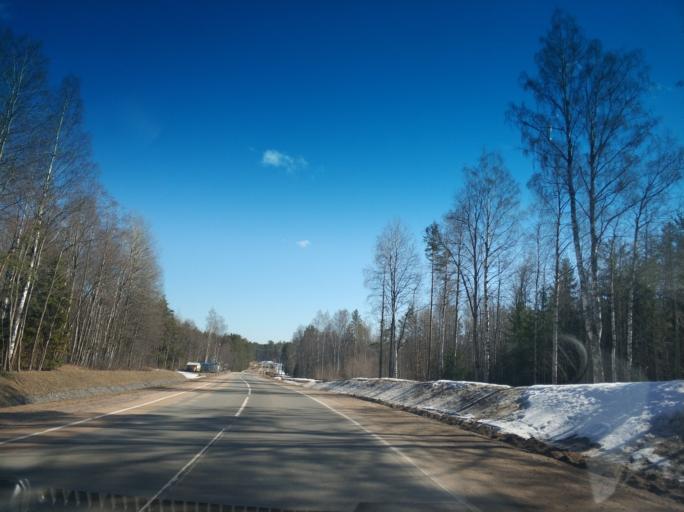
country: RU
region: Leningrad
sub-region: Vsevolzhskij Rajon
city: Vaskelovo
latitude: 60.4261
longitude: 30.2481
